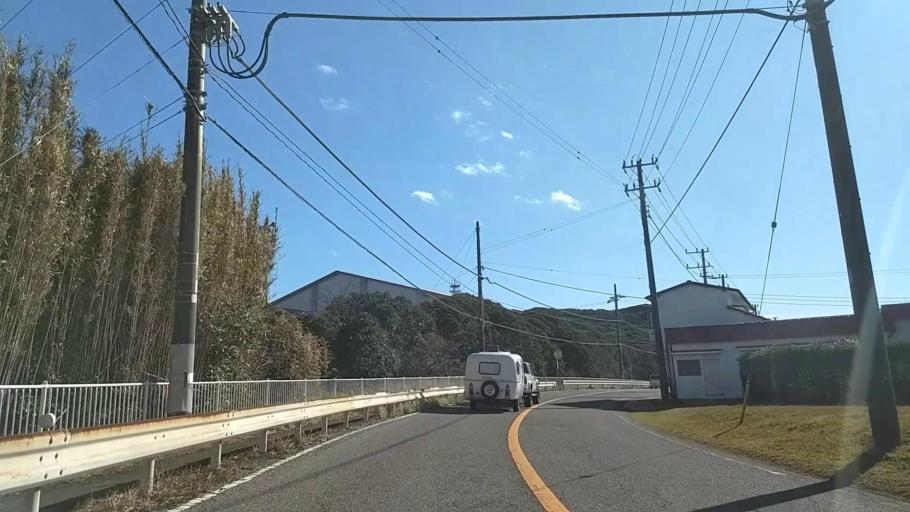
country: JP
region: Chiba
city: Tateyama
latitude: 34.9416
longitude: 139.8396
